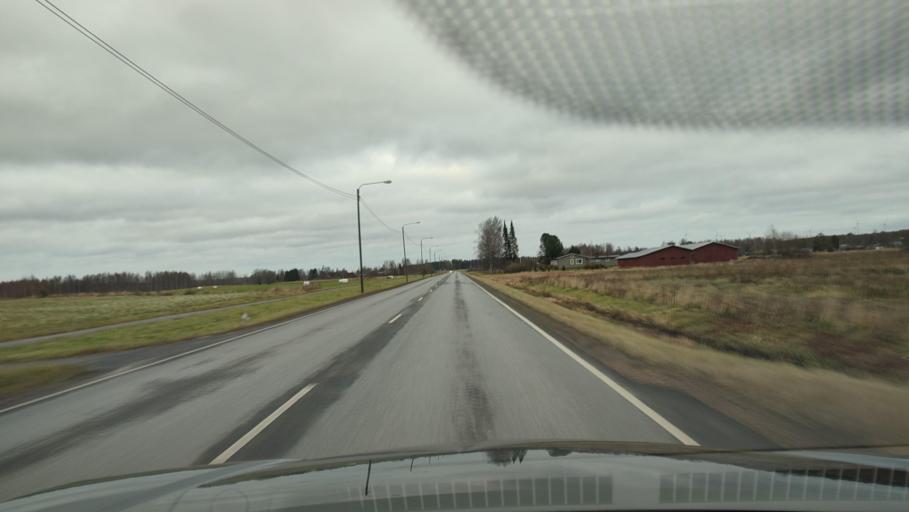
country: FI
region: Southern Ostrobothnia
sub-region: Seinaejoki
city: Kurikka
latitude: 62.6058
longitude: 22.4196
